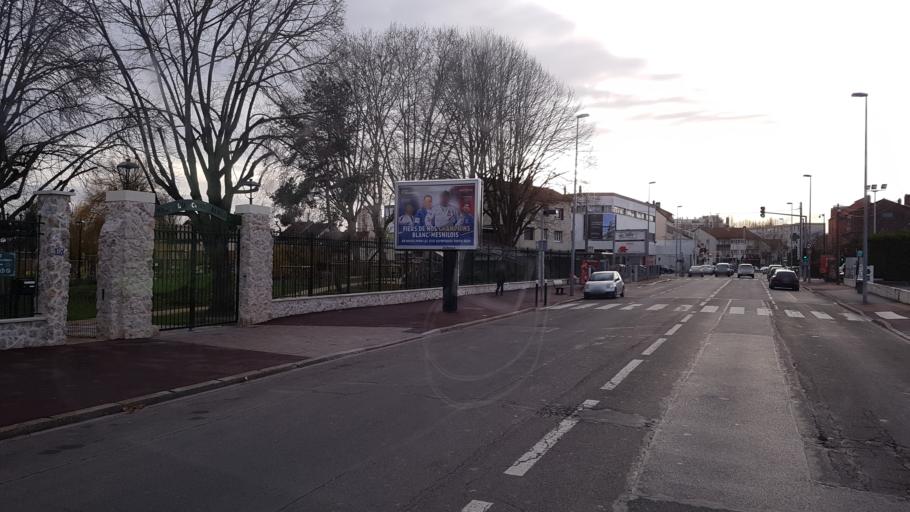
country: FR
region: Ile-de-France
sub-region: Departement de Seine-Saint-Denis
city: Le Blanc-Mesnil
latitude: 48.9251
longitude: 2.4647
